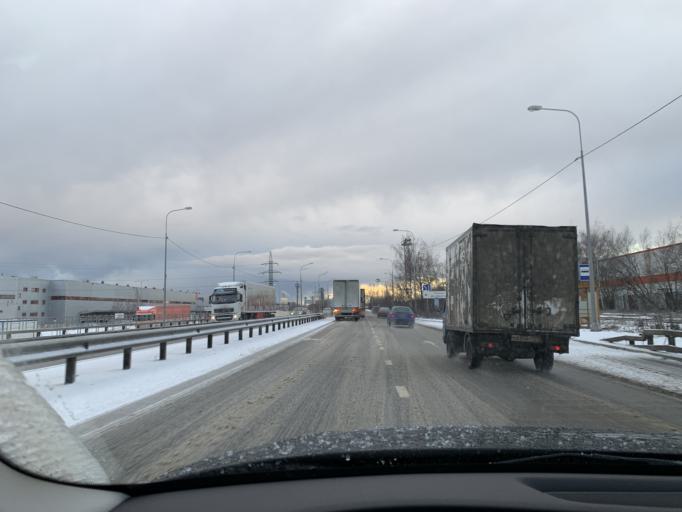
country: RU
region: Moskovskaya
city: Sheremet'yevskiy
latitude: 55.9738
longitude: 37.4954
